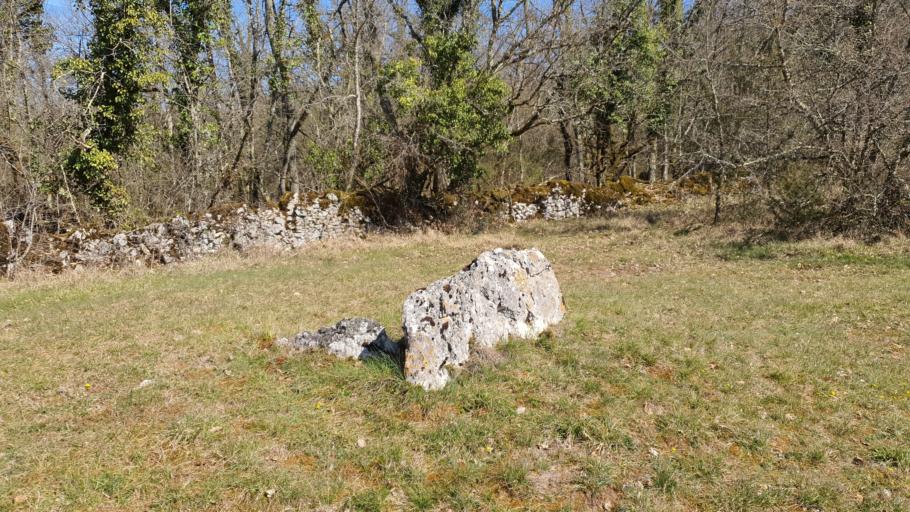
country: FR
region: Midi-Pyrenees
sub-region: Departement du Lot
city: Gramat
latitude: 44.7409
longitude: 1.7647
